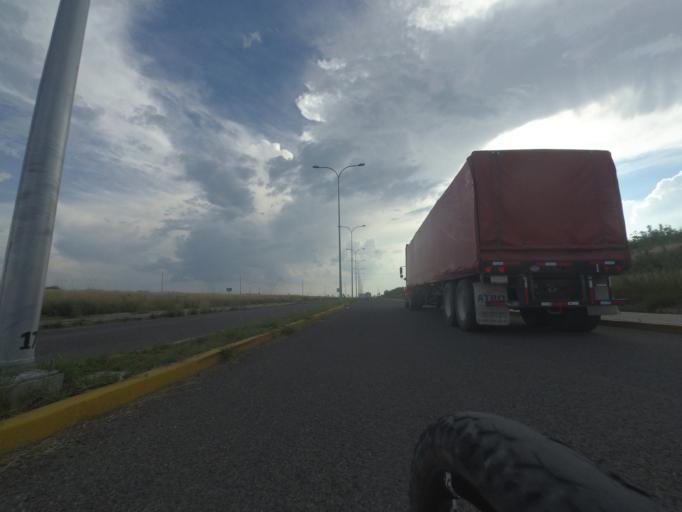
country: MX
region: Aguascalientes
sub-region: Aguascalientes
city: Penuelas (El Cienegal)
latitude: 21.7287
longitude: -102.2854
